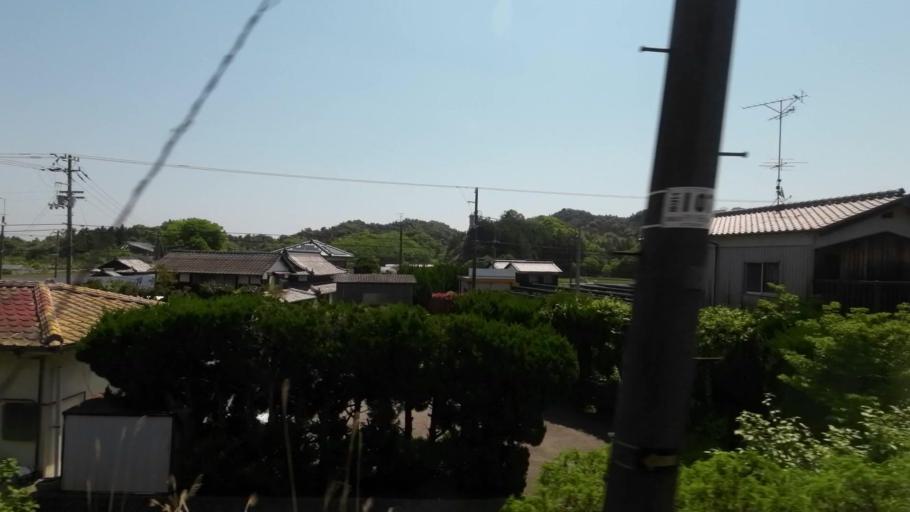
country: JP
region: Ehime
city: Saijo
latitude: 33.9883
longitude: 133.0522
